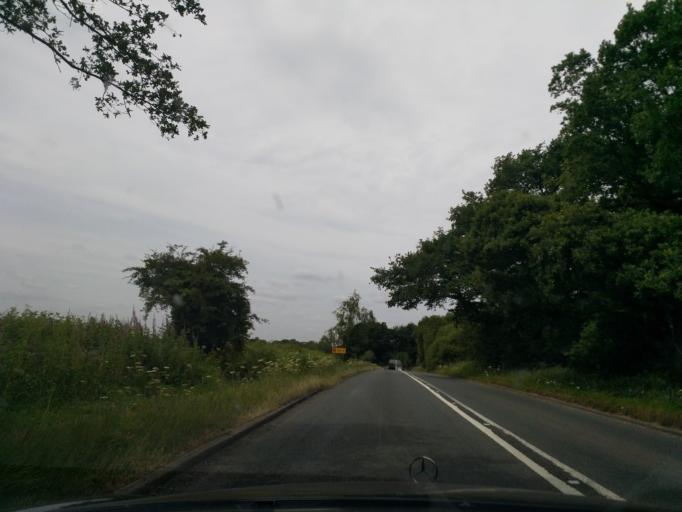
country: GB
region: England
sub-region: Solihull
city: Balsall Common
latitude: 52.3764
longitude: -1.6362
